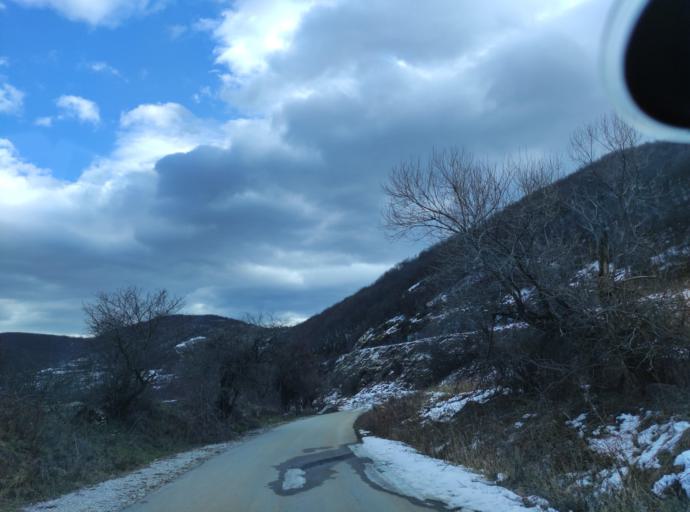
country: BG
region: Montana
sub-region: Obshtina Chiprovtsi
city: Chiprovtsi
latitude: 43.3791
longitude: 22.8647
